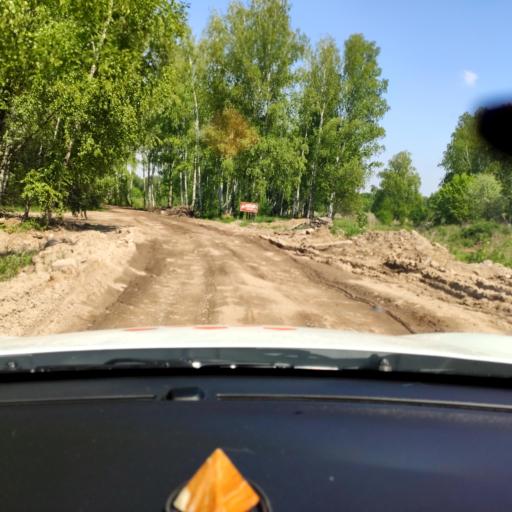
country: RU
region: Tatarstan
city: Stolbishchi
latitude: 55.7074
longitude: 49.1865
